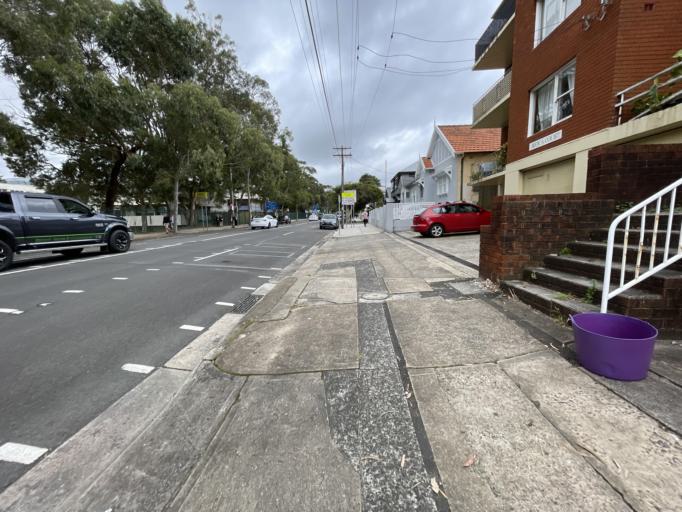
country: AU
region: New South Wales
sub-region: Randwick
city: Randwick
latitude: -33.9226
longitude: 151.2401
